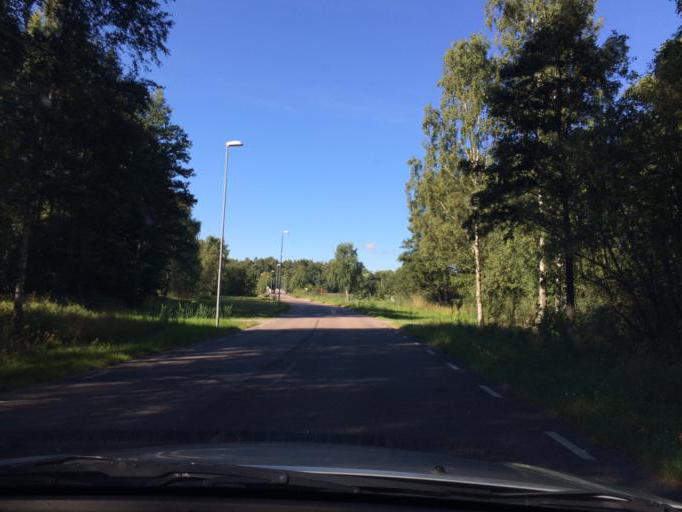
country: SE
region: Vaestmanland
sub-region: Vasteras
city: Vasteras
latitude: 59.5819
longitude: 16.6146
